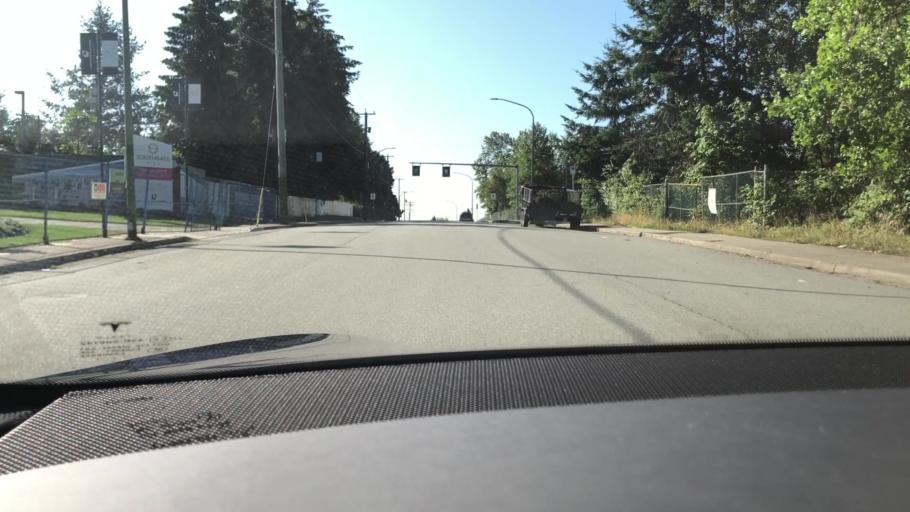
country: CA
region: British Columbia
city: New Westminster
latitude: 49.2103
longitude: -122.9513
